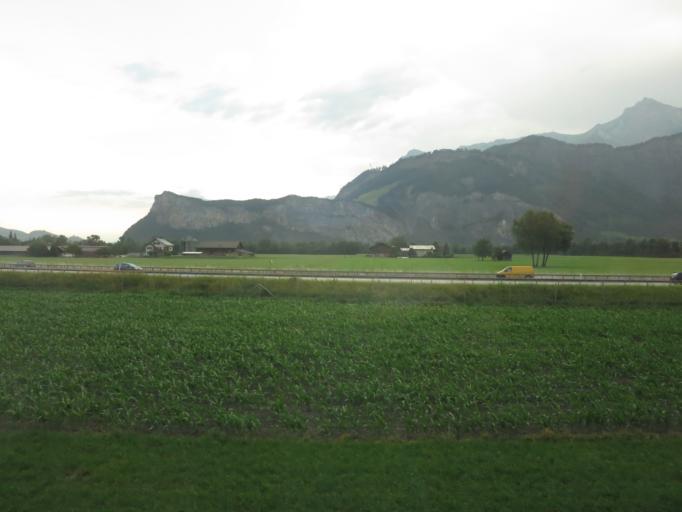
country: CH
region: Saint Gallen
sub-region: Wahlkreis Sarganserland
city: Sargans
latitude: 47.0328
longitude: 9.4662
